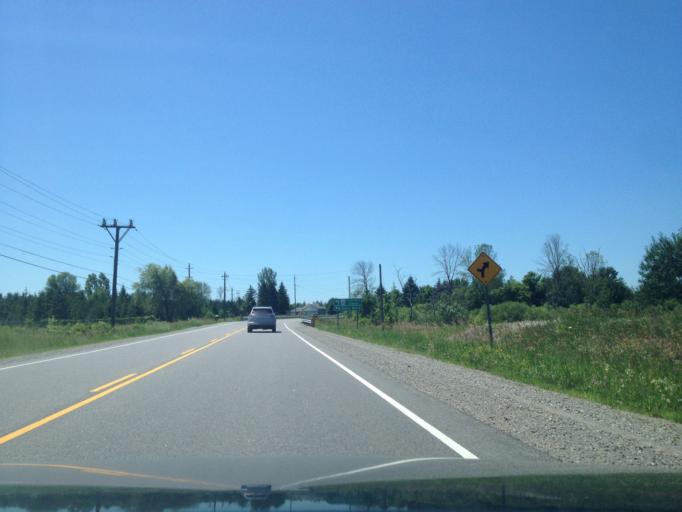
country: CA
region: Ontario
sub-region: Wellington County
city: Guelph
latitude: 43.6041
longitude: -80.1134
